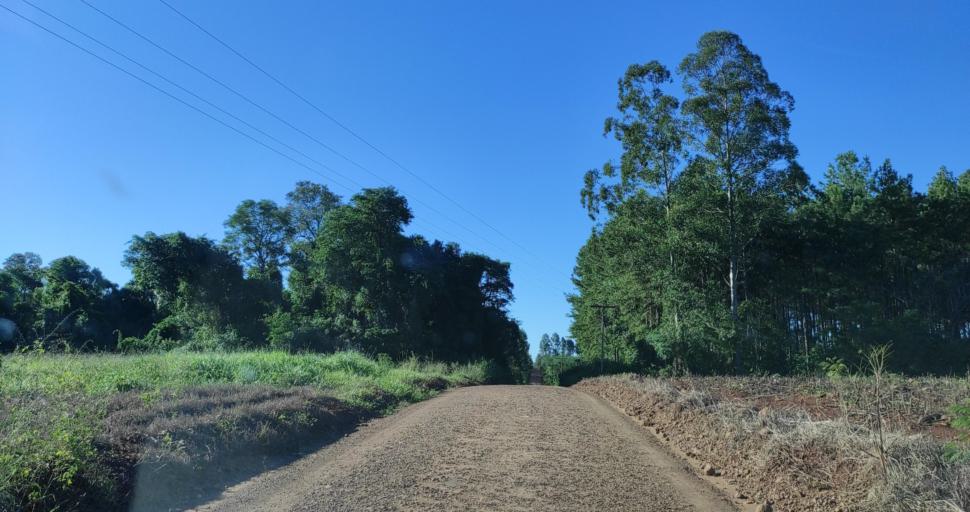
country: AR
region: Misiones
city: Capiovi
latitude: -26.8852
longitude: -54.9968
